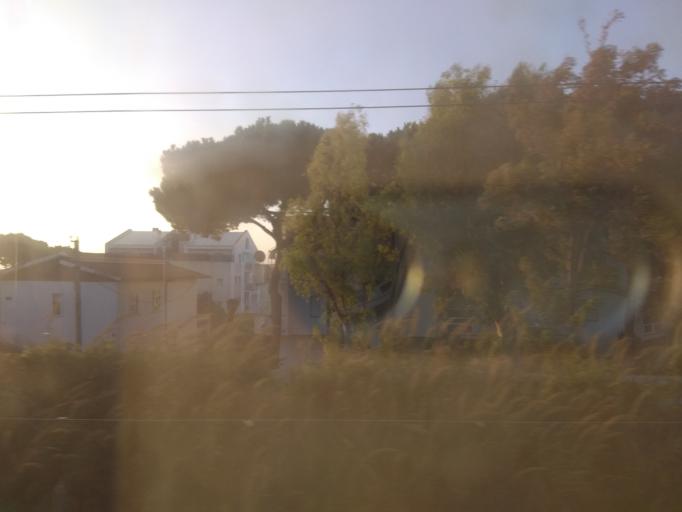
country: IT
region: Latium
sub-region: Citta metropolitana di Roma Capitale
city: Santa Marinella
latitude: 42.0349
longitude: 11.8562
